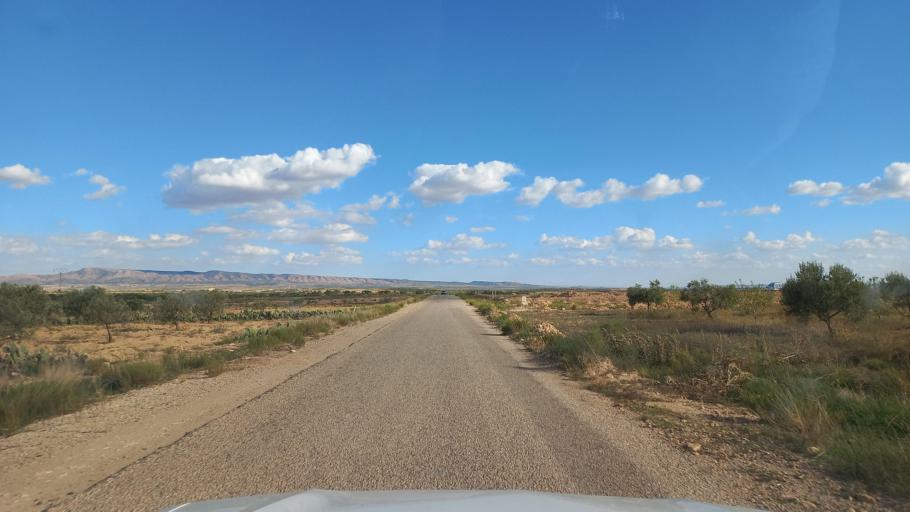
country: TN
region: Al Qasrayn
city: Sbiba
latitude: 35.3911
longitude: 9.0252
